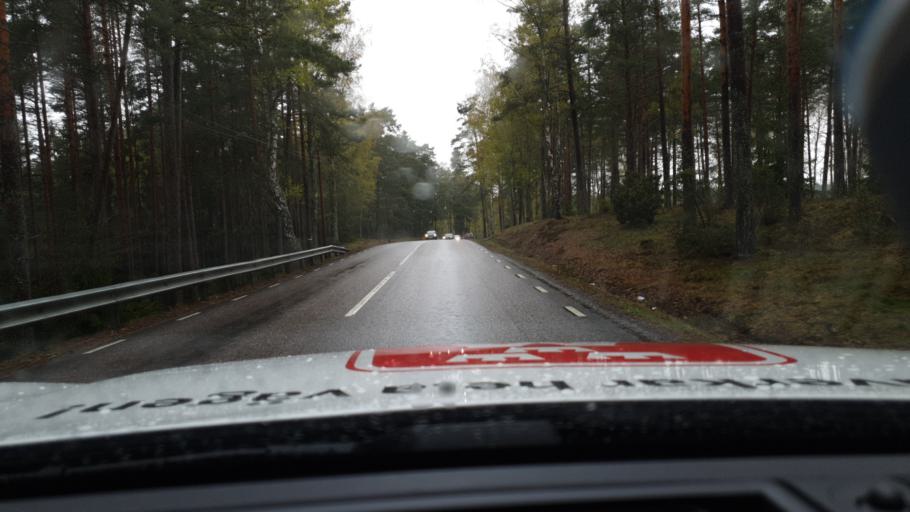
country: SE
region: Stockholm
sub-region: Botkyrka Kommun
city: Eriksberg
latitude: 59.2313
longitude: 17.7830
